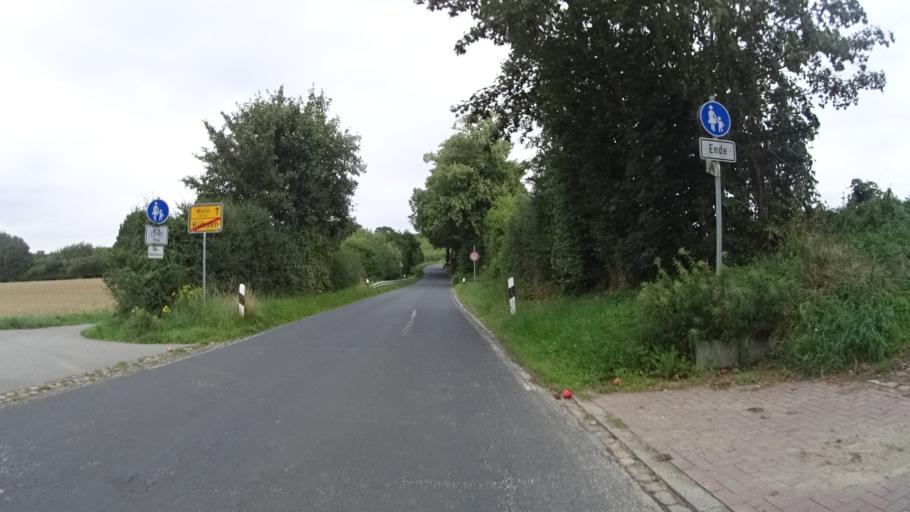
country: DE
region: Schleswig-Holstein
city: Kuhsen
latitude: 53.6831
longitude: 10.6198
